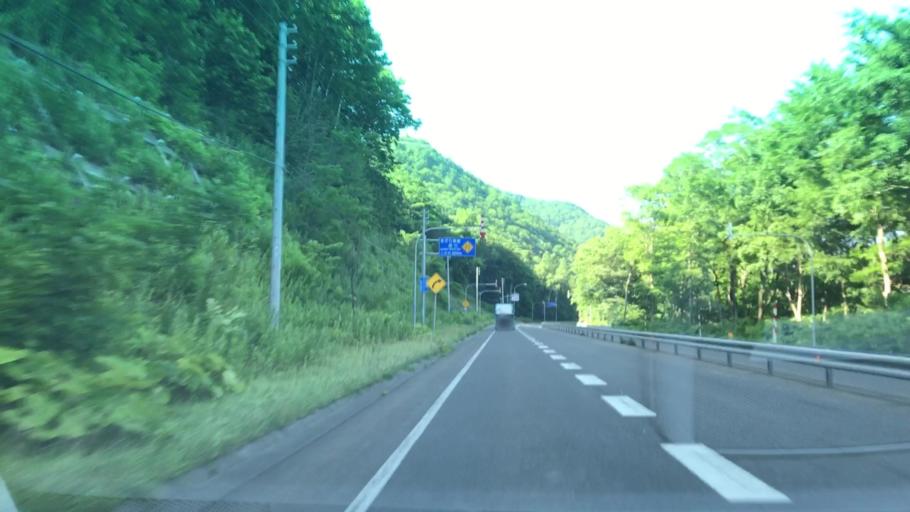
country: JP
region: Hokkaido
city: Iwanai
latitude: 43.0162
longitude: 140.6663
